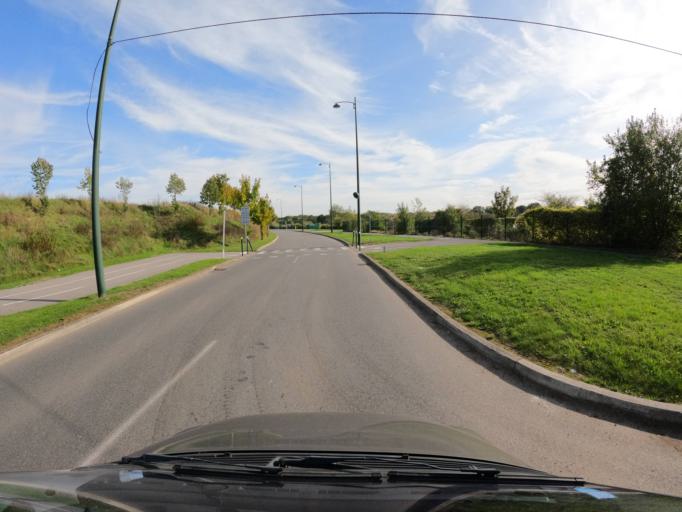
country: FR
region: Ile-de-France
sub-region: Departement du Val-de-Marne
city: La Queue-en-Brie
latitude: 48.7758
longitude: 2.5863
